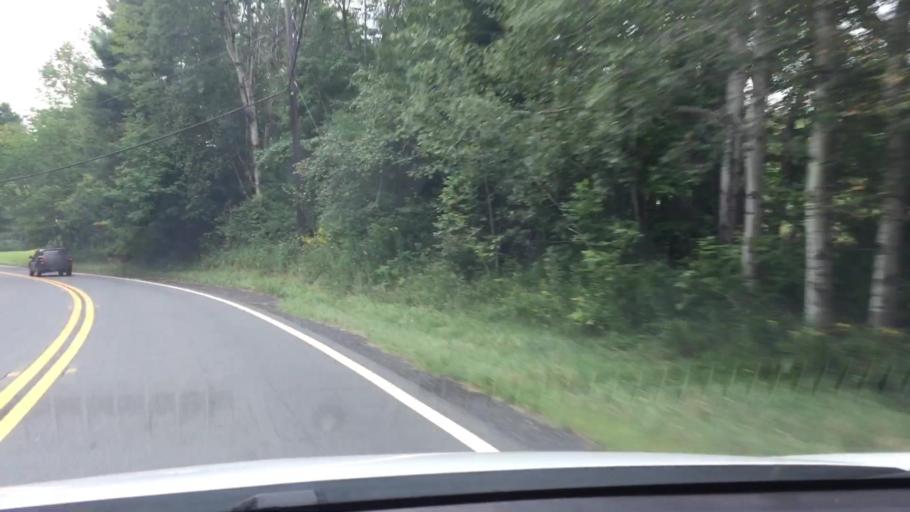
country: US
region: Massachusetts
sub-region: Berkshire County
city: Becket
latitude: 42.3712
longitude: -73.1172
